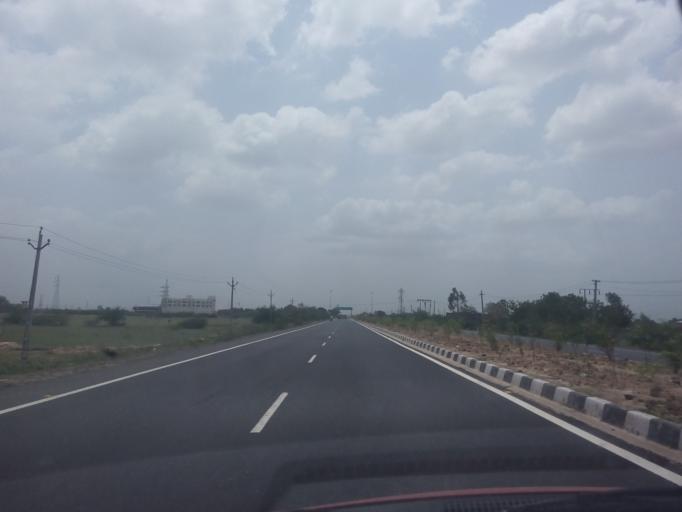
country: IN
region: Gujarat
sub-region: Ahmadabad
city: Mandal
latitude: 23.0979
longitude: 72.0561
